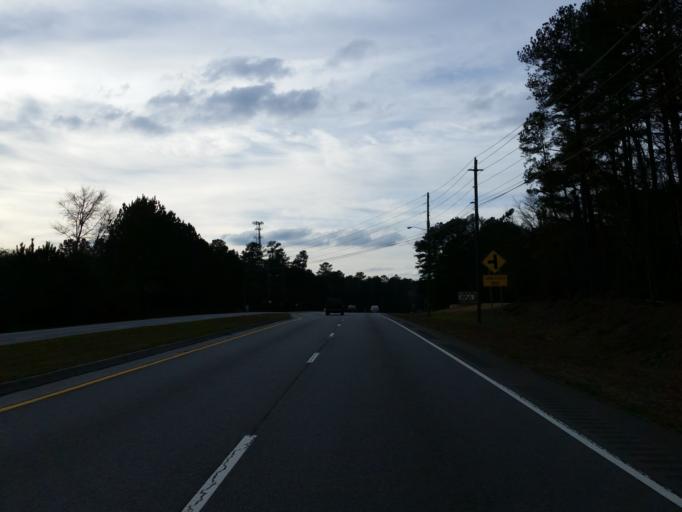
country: US
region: Georgia
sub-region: Cobb County
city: Powder Springs
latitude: 33.8971
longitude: -84.6433
